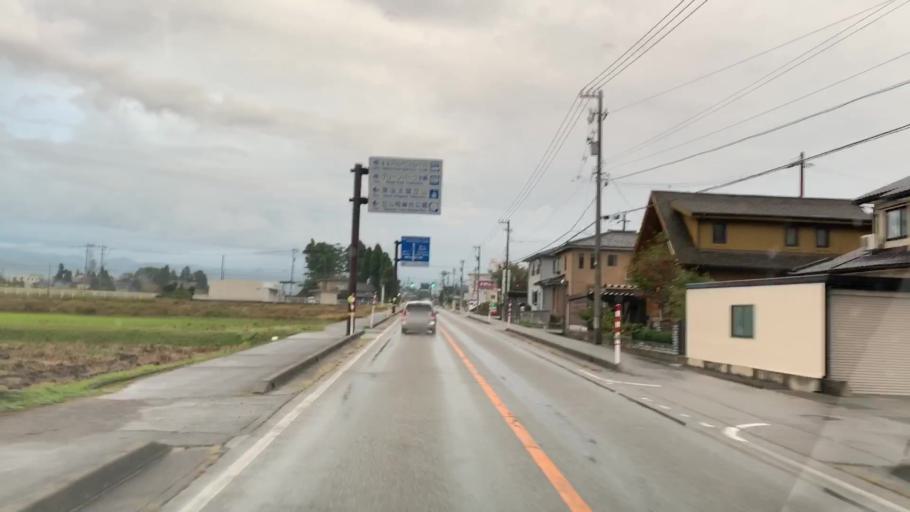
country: JP
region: Toyama
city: Kamiichi
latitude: 36.6689
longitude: 137.3275
